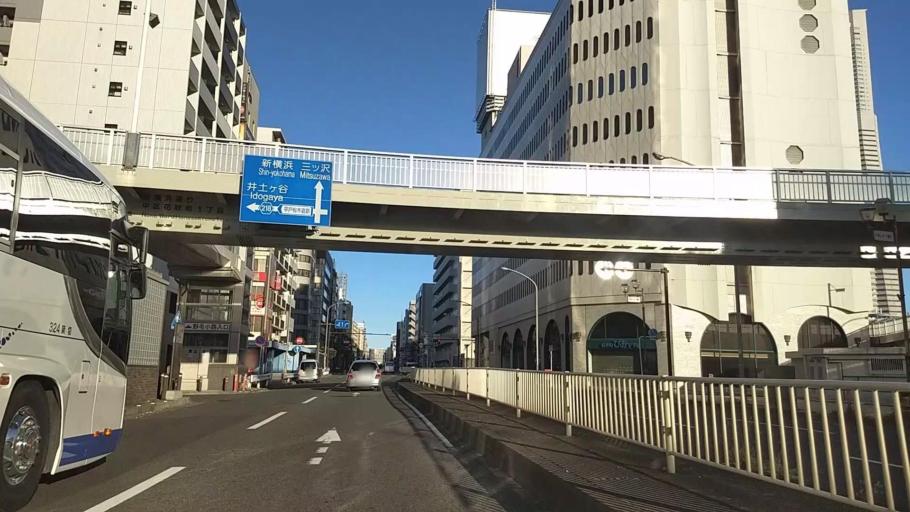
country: JP
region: Kanagawa
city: Yokohama
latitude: 35.4493
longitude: 139.6310
